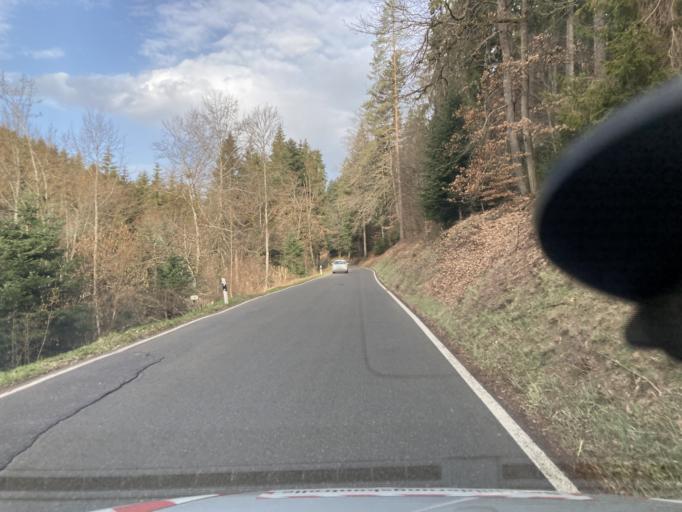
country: DE
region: Baden-Wuerttemberg
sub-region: Karlsruhe Region
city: Bad Teinach-Zavelstein
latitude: 48.6783
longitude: 8.6522
